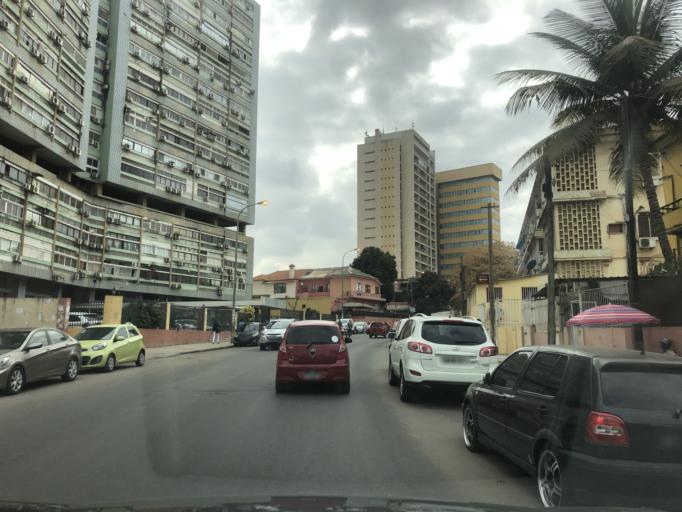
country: AO
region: Luanda
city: Luanda
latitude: -8.8242
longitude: 13.2318
